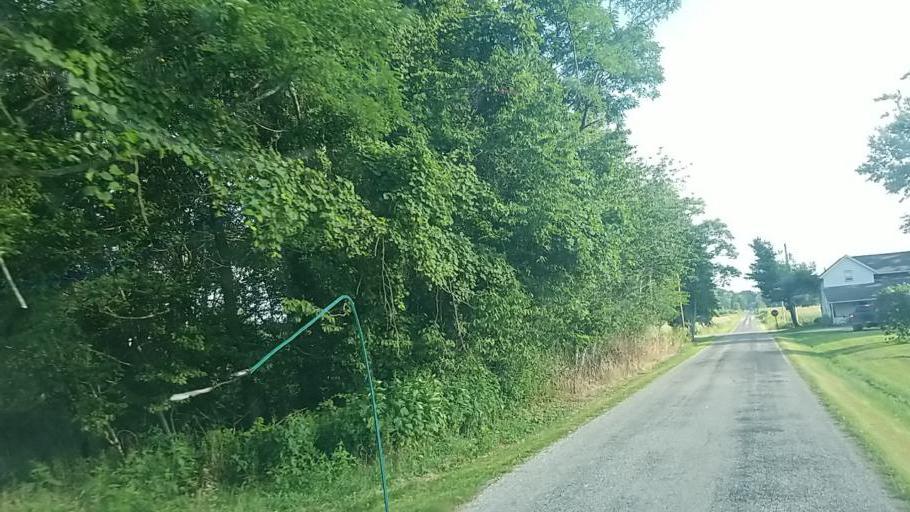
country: US
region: Ohio
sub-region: Wayne County
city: West Salem
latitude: 40.8942
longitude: -82.1929
